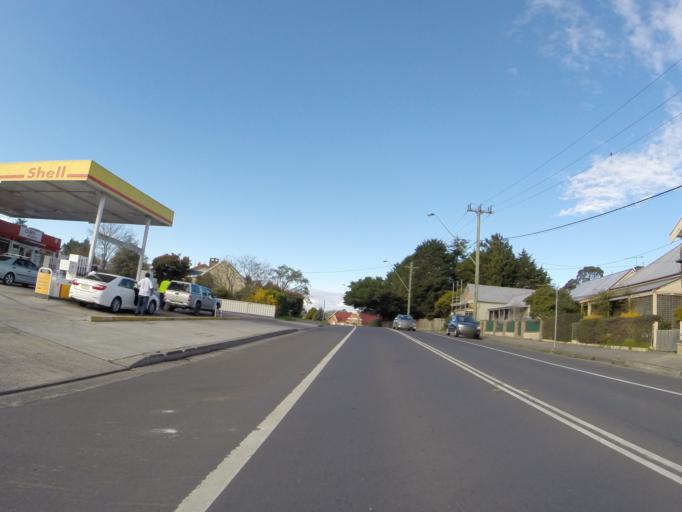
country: AU
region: New South Wales
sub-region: Wingecarribee
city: Moss Vale
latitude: -34.5534
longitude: 150.3645
